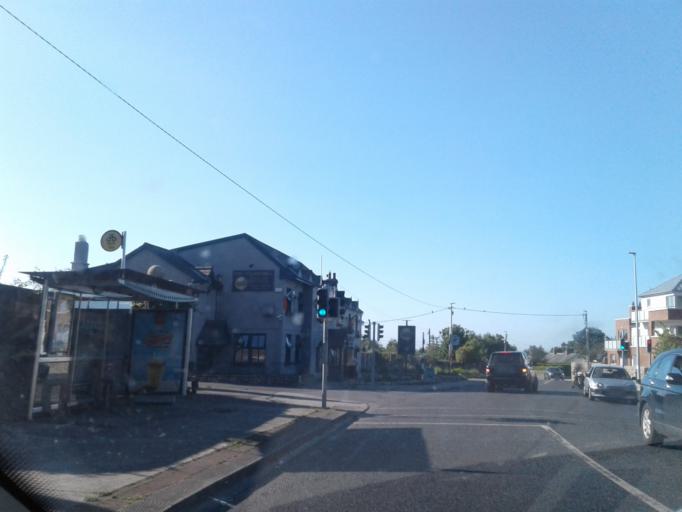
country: IE
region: Leinster
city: Foxrock
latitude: 53.2391
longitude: -6.1962
